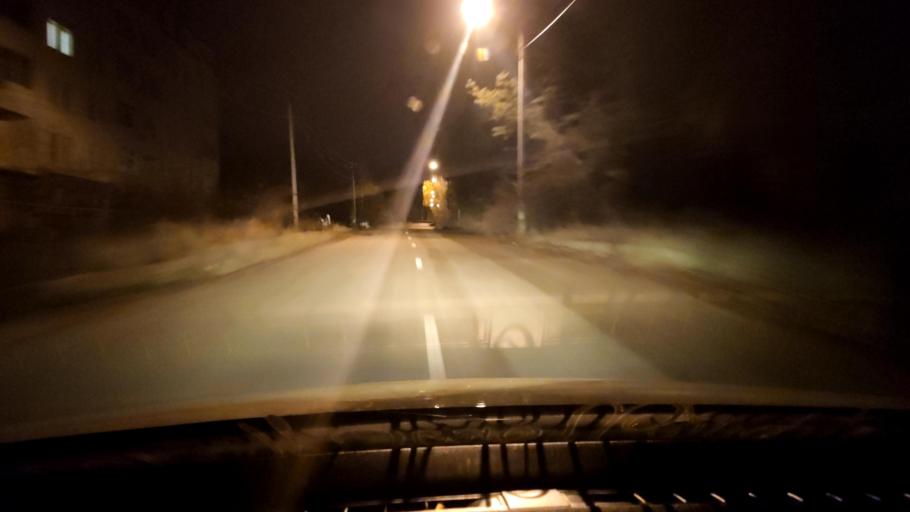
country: RU
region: Voronezj
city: Pridonskoy
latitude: 51.6993
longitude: 39.1053
